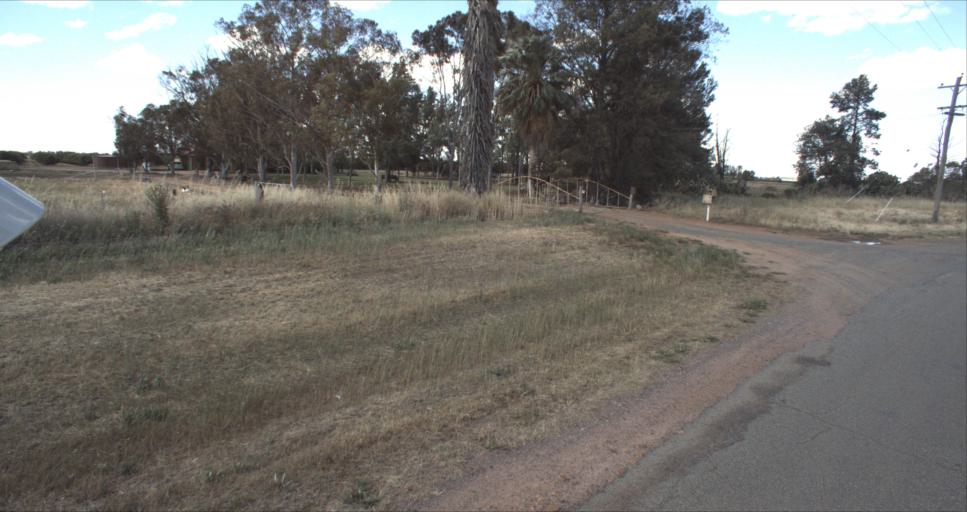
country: AU
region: New South Wales
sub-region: Leeton
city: Leeton
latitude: -34.5127
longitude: 146.2444
